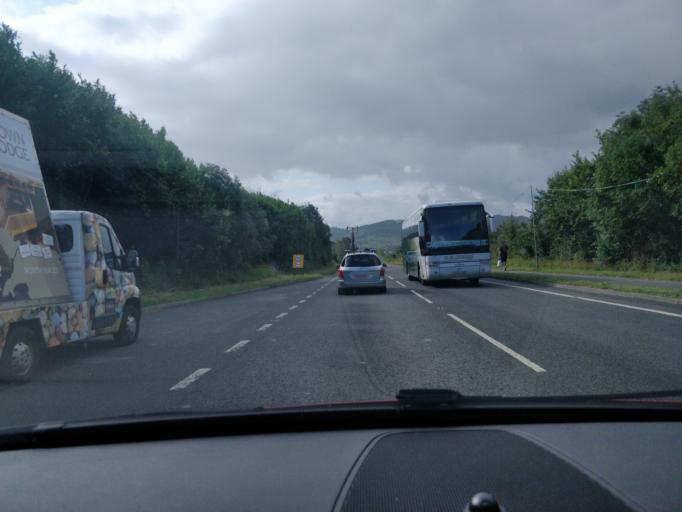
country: GB
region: Wales
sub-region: Conwy
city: Llanrwst
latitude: 53.1254
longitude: -3.7830
